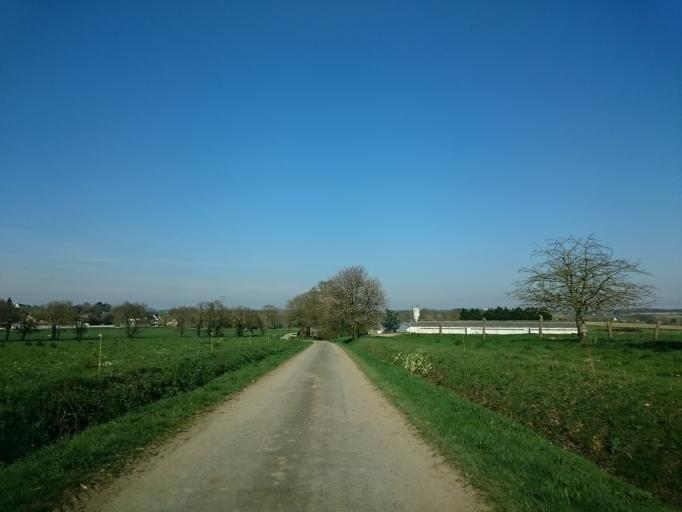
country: FR
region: Brittany
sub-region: Departement d'Ille-et-Vilaine
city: Chanteloup
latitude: 47.9560
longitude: -1.6186
